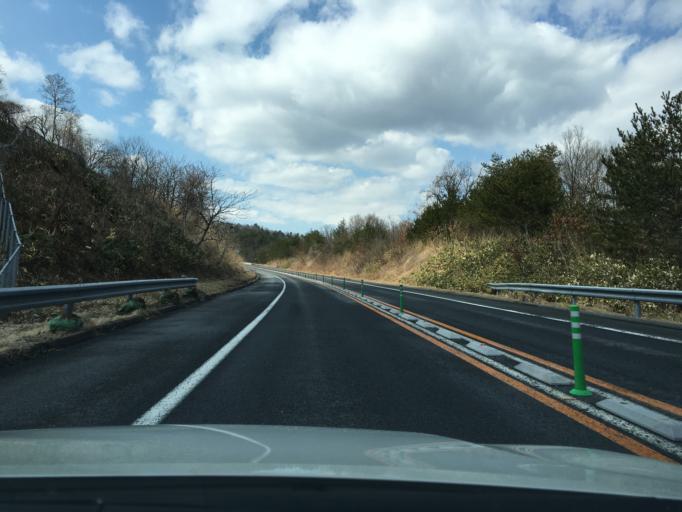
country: JP
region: Yamagata
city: Sagae
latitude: 38.4006
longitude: 140.2080
